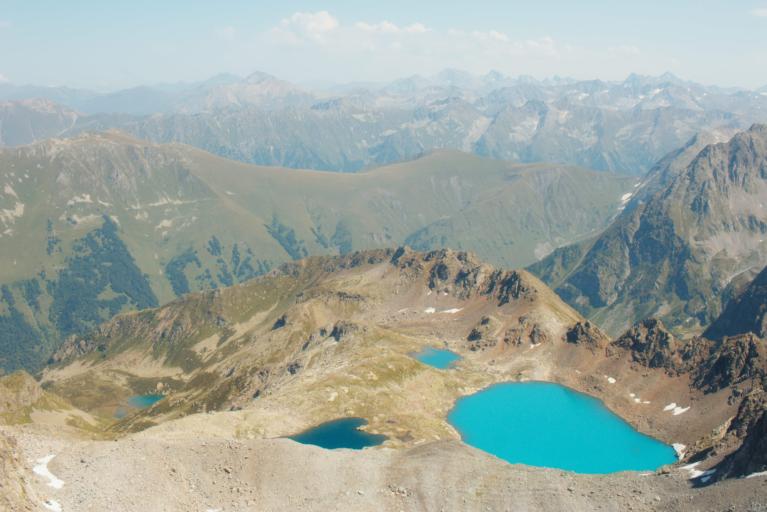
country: RU
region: Karachayevo-Cherkesiya
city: Nizhniy Arkhyz
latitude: 43.4515
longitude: 41.2181
